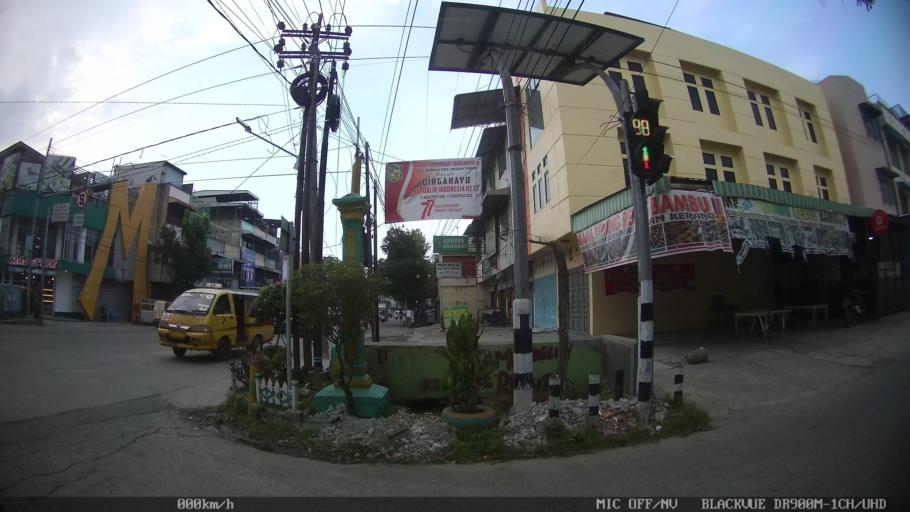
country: ID
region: North Sumatra
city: Medan
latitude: 3.6072
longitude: 98.6801
